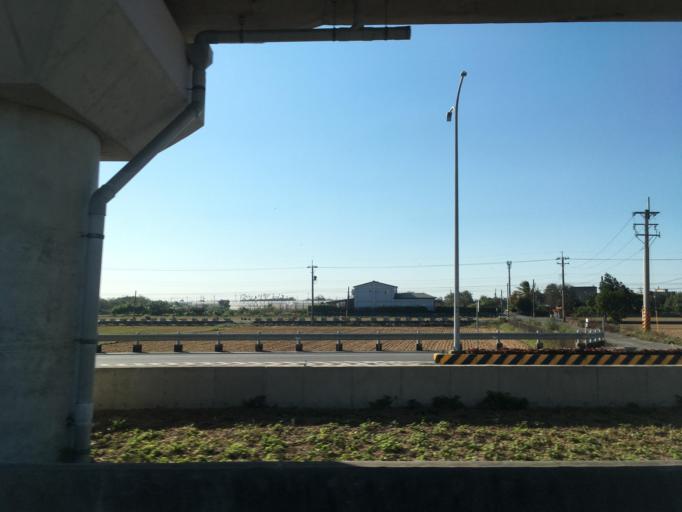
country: TW
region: Taiwan
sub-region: Chiayi
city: Taibao
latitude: 23.4437
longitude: 120.3232
